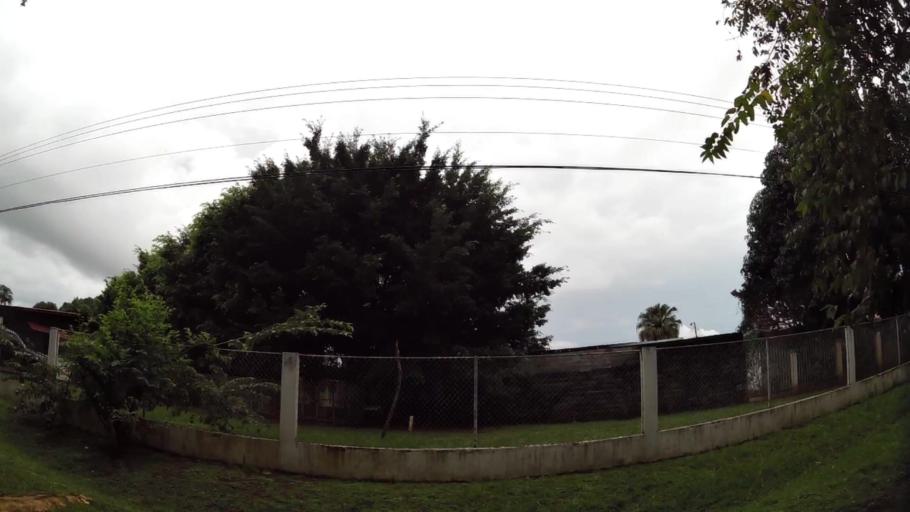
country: PA
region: Chiriqui
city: David
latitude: 8.4166
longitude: -82.4569
